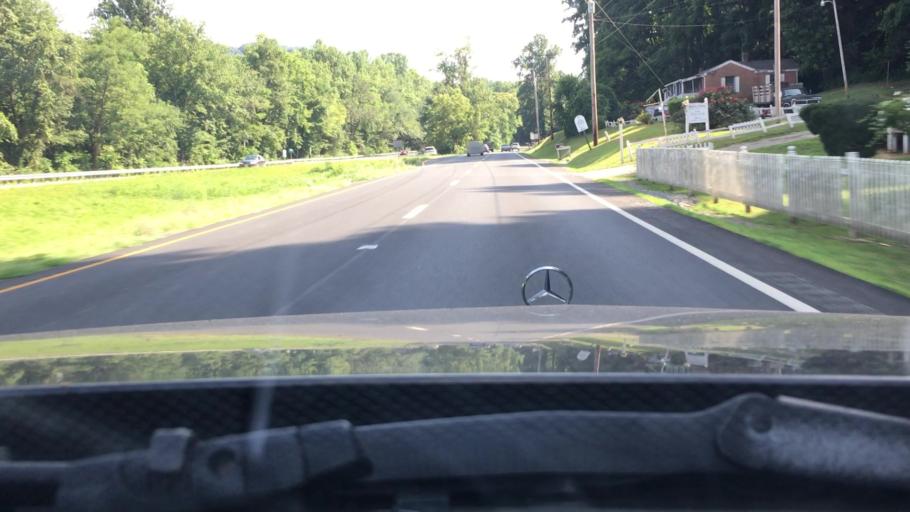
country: US
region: Virginia
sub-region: Albemarle County
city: Crozet
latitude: 37.9510
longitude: -78.6627
